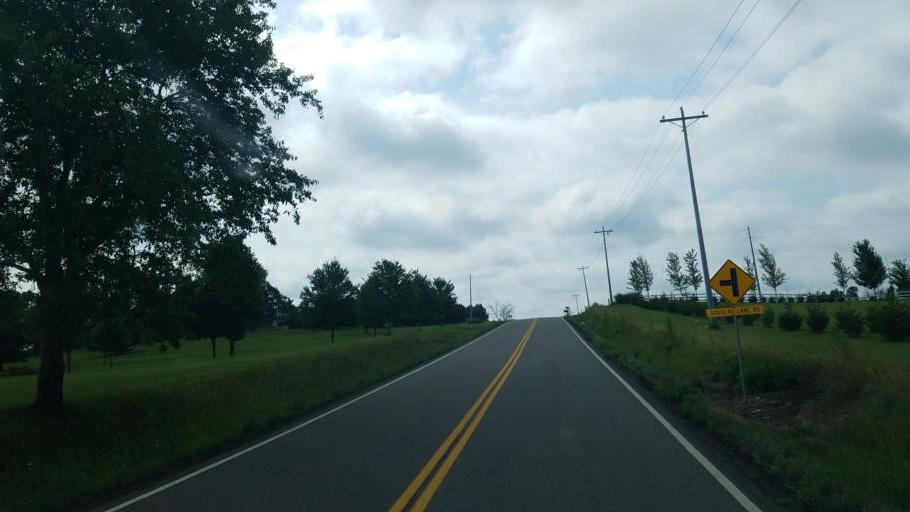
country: US
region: Ohio
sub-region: Licking County
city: Utica
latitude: 40.2427
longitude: -82.5790
